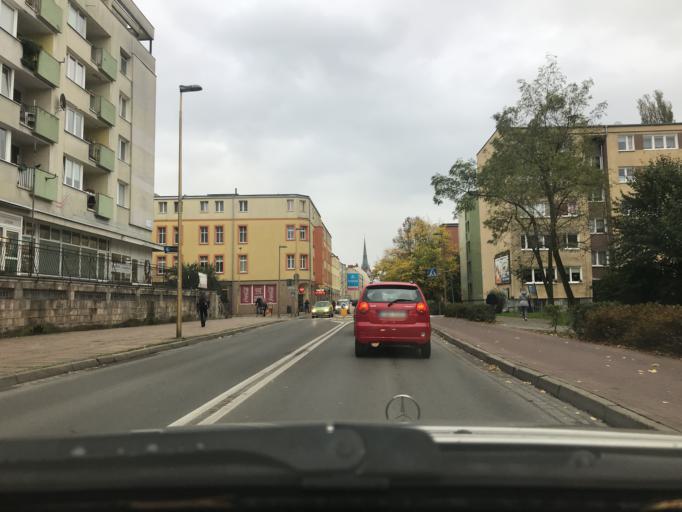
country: PL
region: West Pomeranian Voivodeship
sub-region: Swinoujscie
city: Swinoujscie
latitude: 53.9113
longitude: 14.2425
